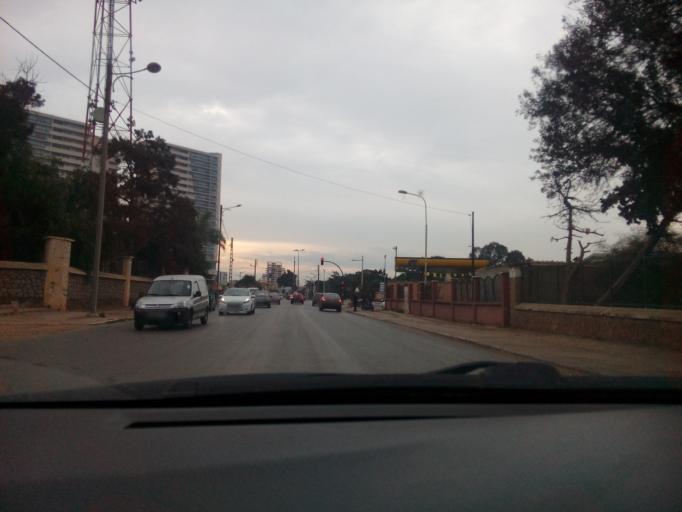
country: DZ
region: Oran
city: Oran
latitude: 35.6826
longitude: -0.6376
